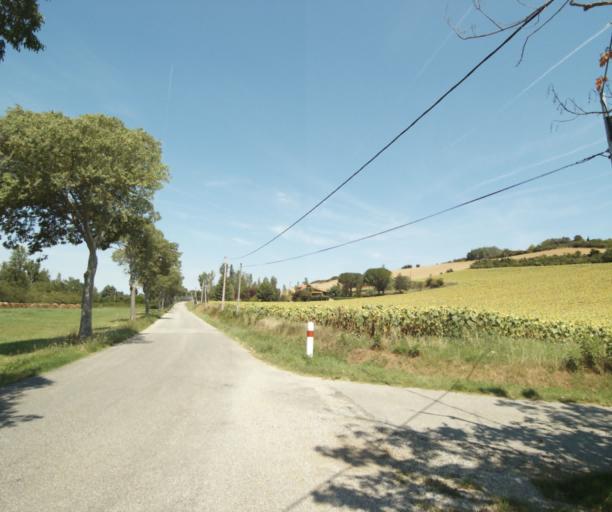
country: FR
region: Midi-Pyrenees
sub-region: Departement de l'Ariege
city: Lezat-sur-Leze
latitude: 43.2830
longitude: 1.3551
